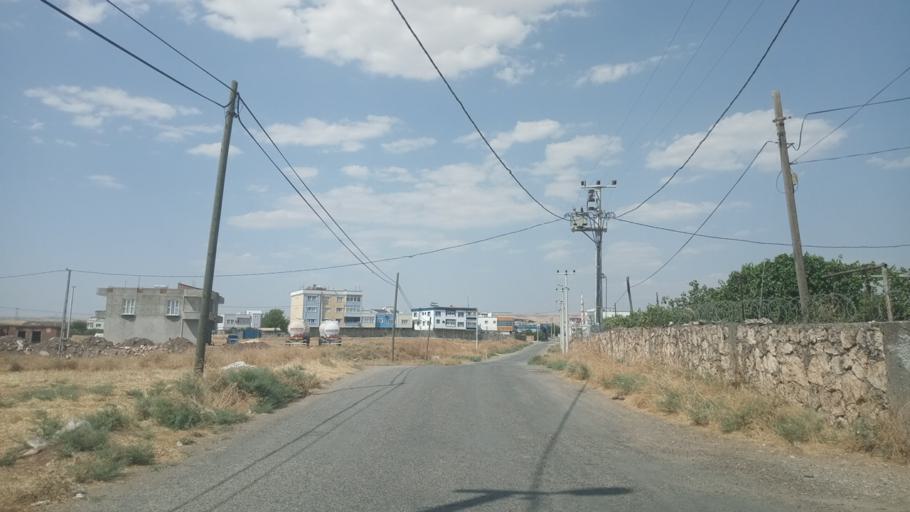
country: TR
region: Batman
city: Binatli
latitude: 37.8432
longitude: 41.2125
